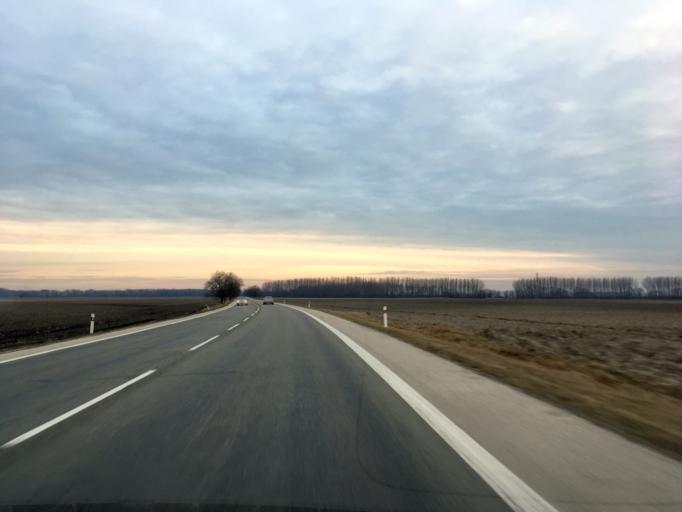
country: SK
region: Trnavsky
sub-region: Okres Dunajska Streda
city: Velky Meder
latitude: 47.9153
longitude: 17.7285
